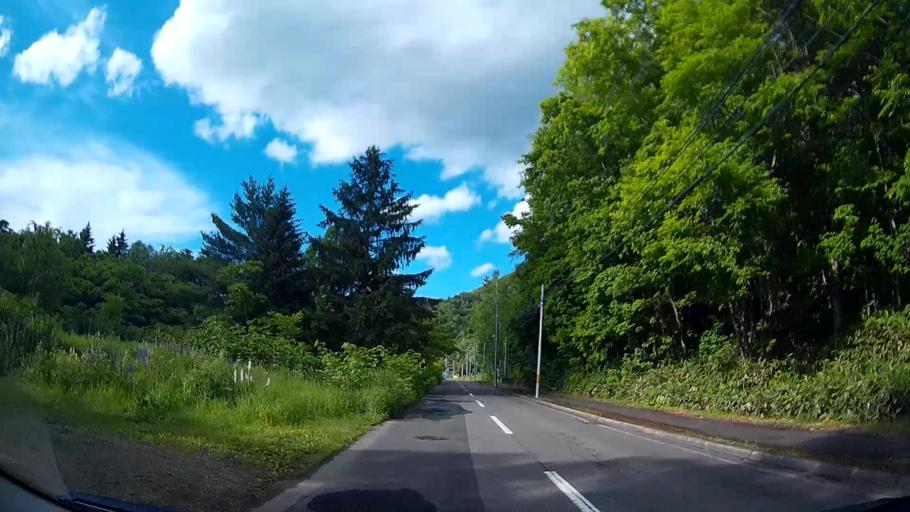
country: JP
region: Hokkaido
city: Sapporo
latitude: 42.9462
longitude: 141.1547
